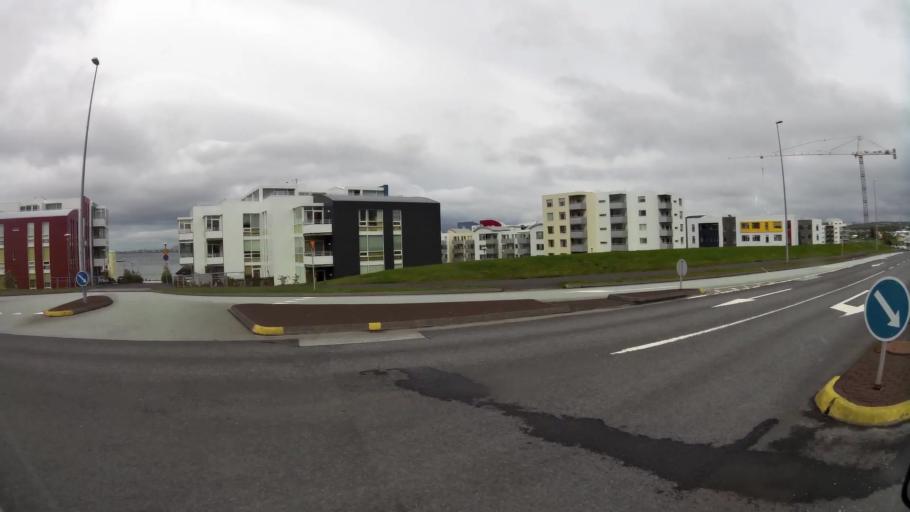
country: IS
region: Capital Region
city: Gardabaer
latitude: 64.0917
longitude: -21.9440
